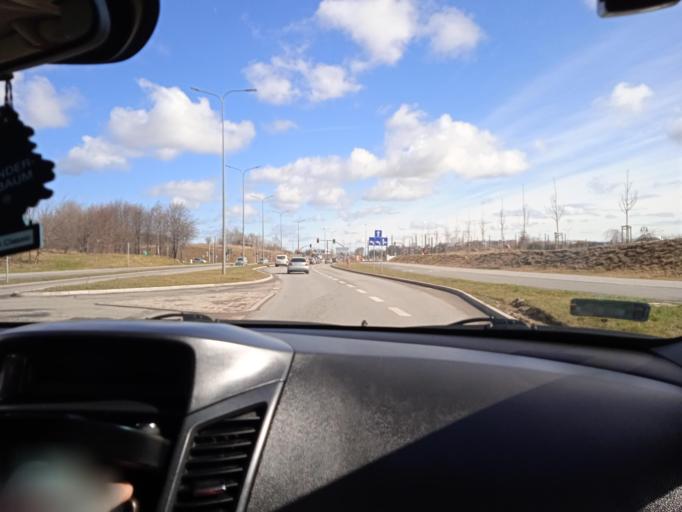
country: PL
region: Pomeranian Voivodeship
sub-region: Powiat gdanski
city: Kowale
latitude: 54.3320
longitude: 18.5671
